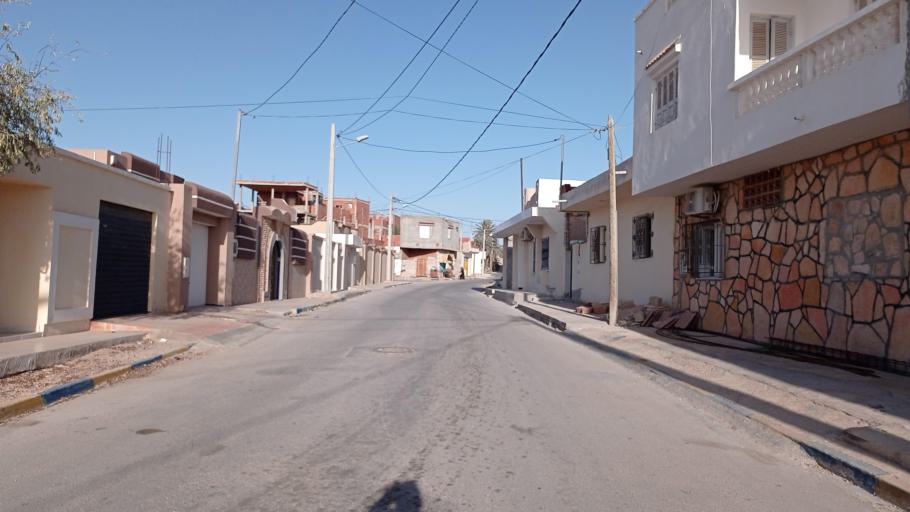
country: TN
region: Qabis
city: Gabes
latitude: 33.8570
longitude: 10.1186
